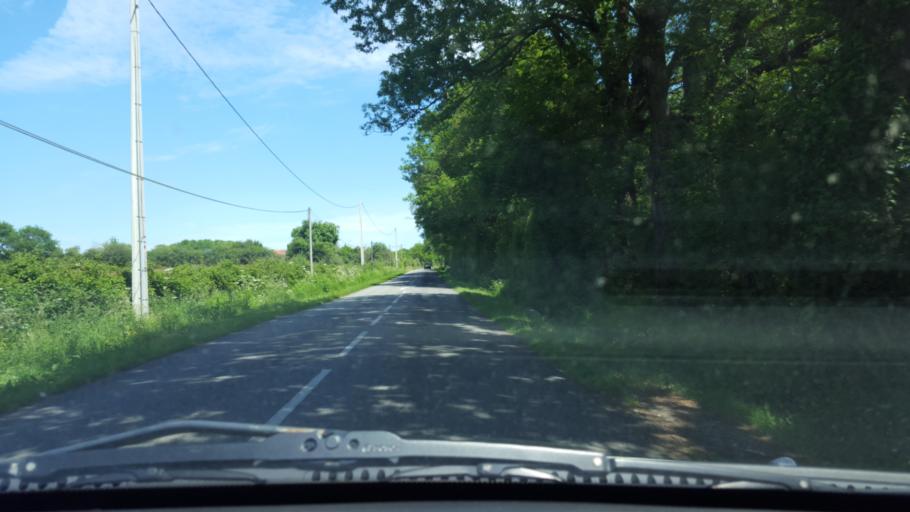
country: FR
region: Pays de la Loire
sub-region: Departement de la Loire-Atlantique
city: Touvois
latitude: 46.9039
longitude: -1.6762
